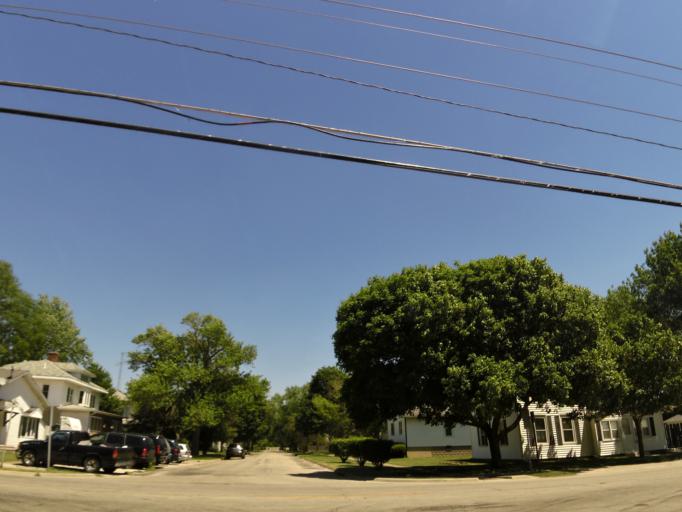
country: US
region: Illinois
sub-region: Livingston County
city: Forrest
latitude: 40.7504
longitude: -88.4108
